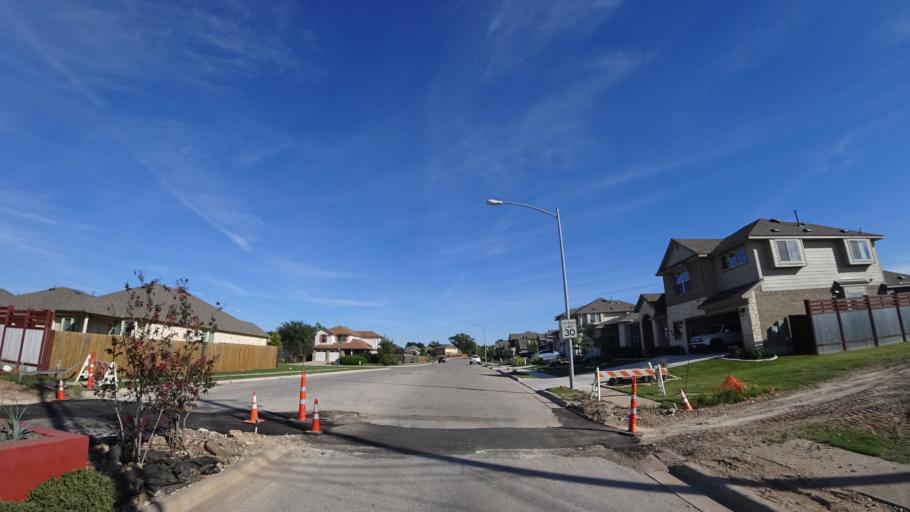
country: US
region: Texas
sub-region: Travis County
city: Austin
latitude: 30.2607
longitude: -97.6733
